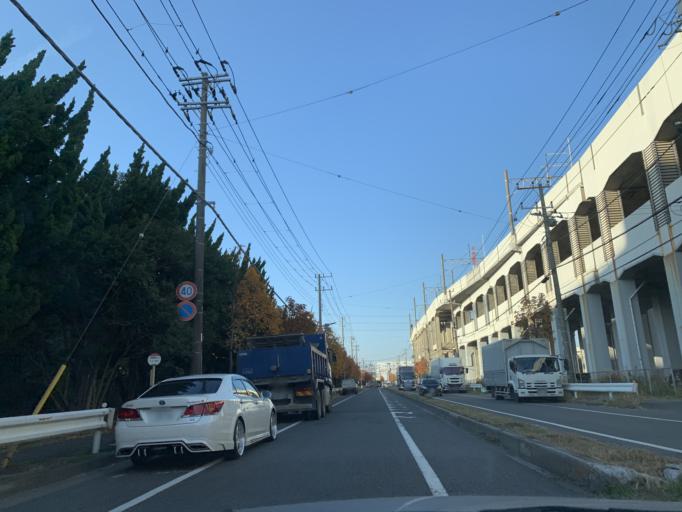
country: JP
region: Chiba
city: Funabashi
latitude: 35.6947
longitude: 139.9559
